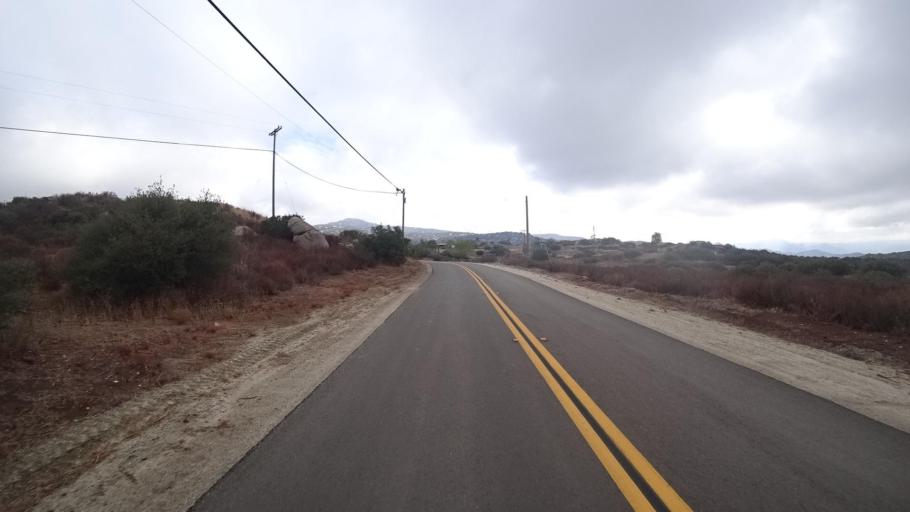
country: MX
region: Baja California
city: Tecate
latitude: 32.6030
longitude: -116.5804
